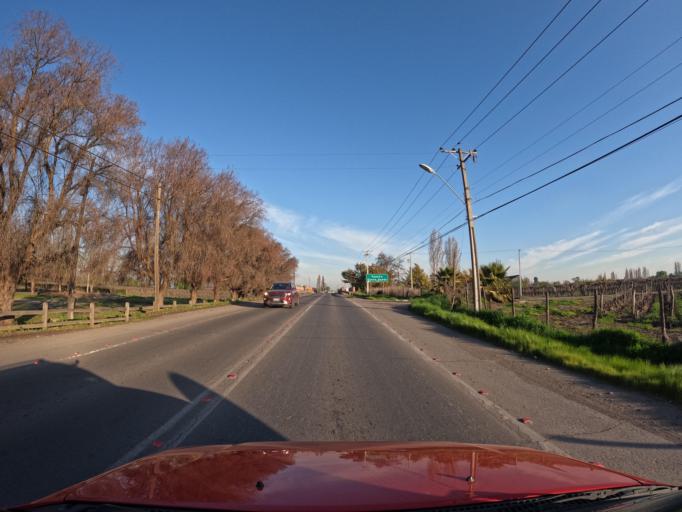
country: CL
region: Maule
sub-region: Provincia de Curico
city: Curico
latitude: -34.9549
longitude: -71.2545
